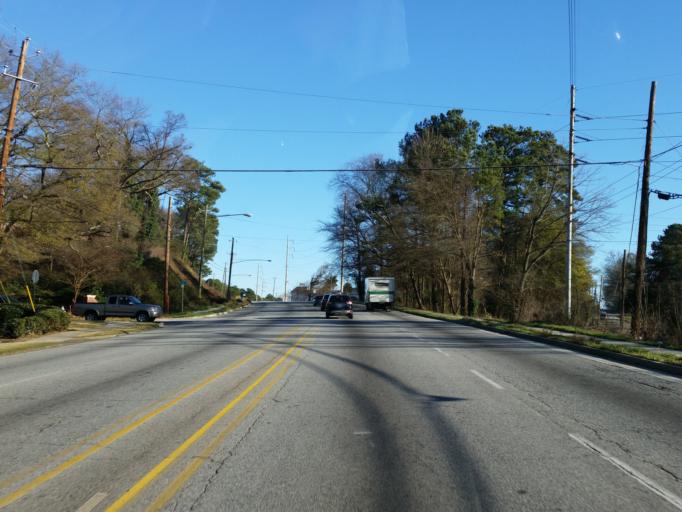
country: US
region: Georgia
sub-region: Cobb County
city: Vinings
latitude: 33.8164
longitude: -84.4460
